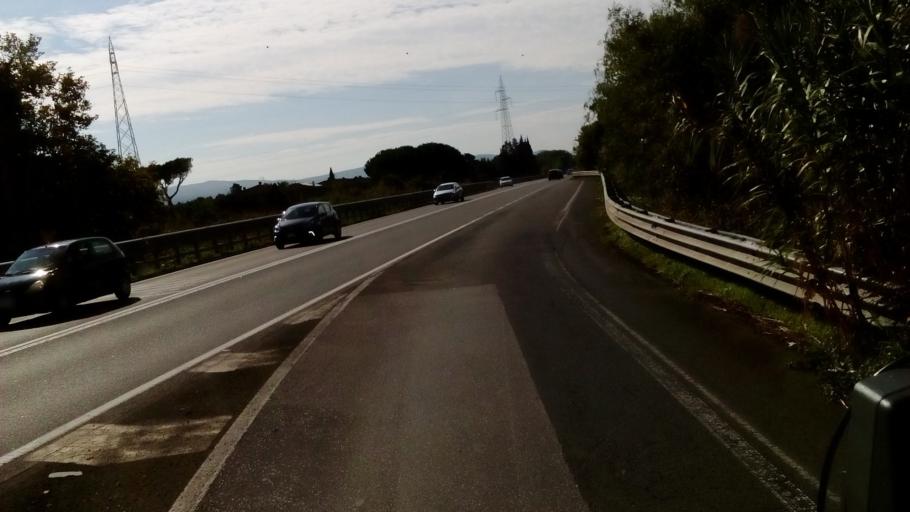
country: IT
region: Tuscany
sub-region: Provincia di Livorno
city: Livorno
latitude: 43.5830
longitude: 10.3496
